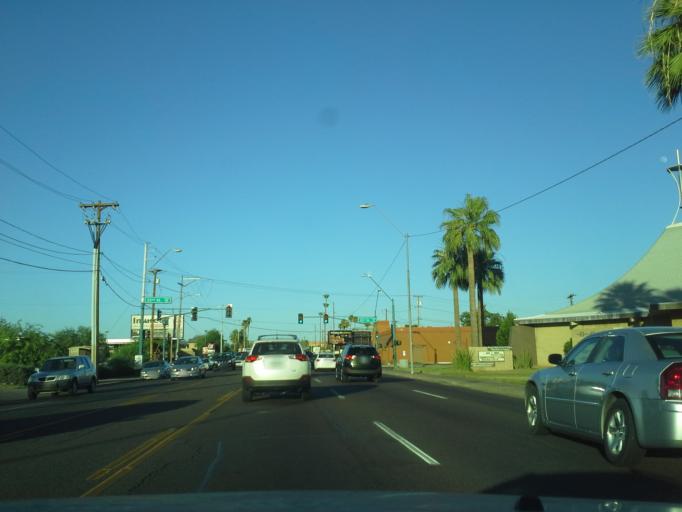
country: US
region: Arizona
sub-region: Maricopa County
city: Phoenix
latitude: 33.4803
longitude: -112.0354
